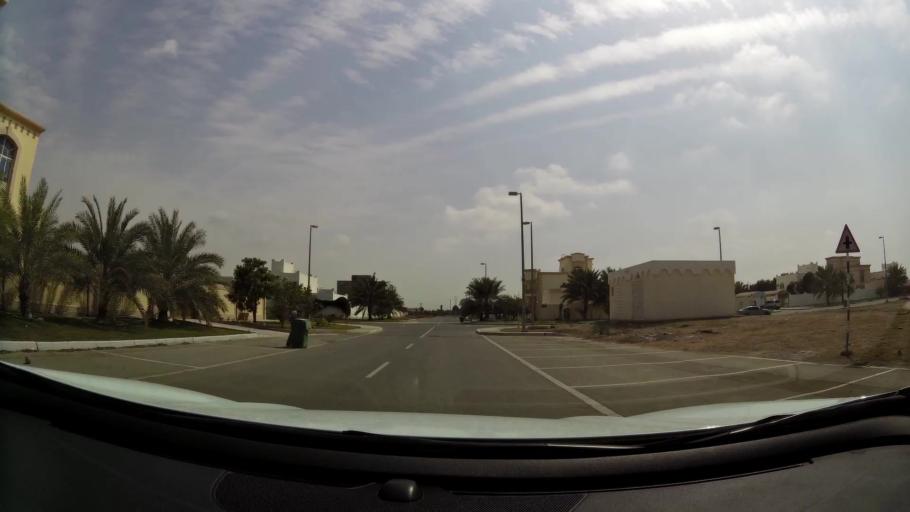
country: AE
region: Abu Dhabi
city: Abu Dhabi
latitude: 24.5502
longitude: 54.6362
